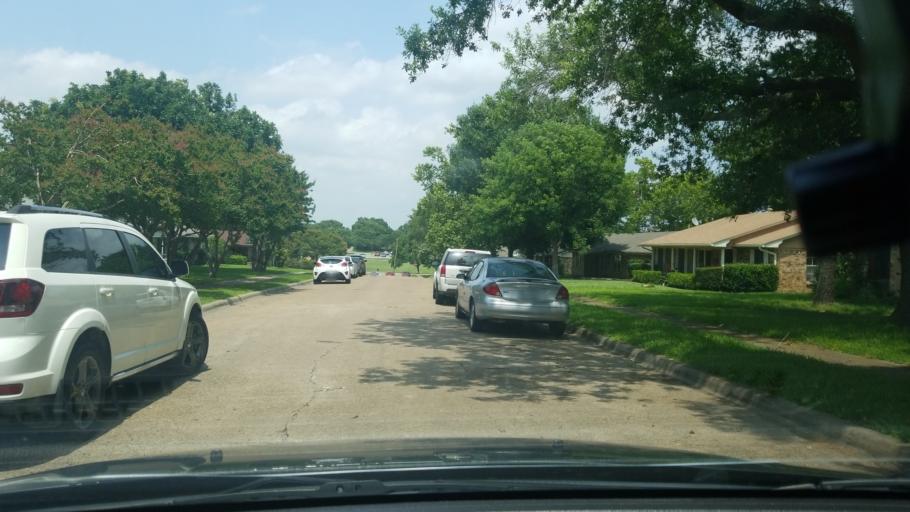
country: US
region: Texas
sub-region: Dallas County
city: Mesquite
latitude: 32.8037
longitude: -96.6388
